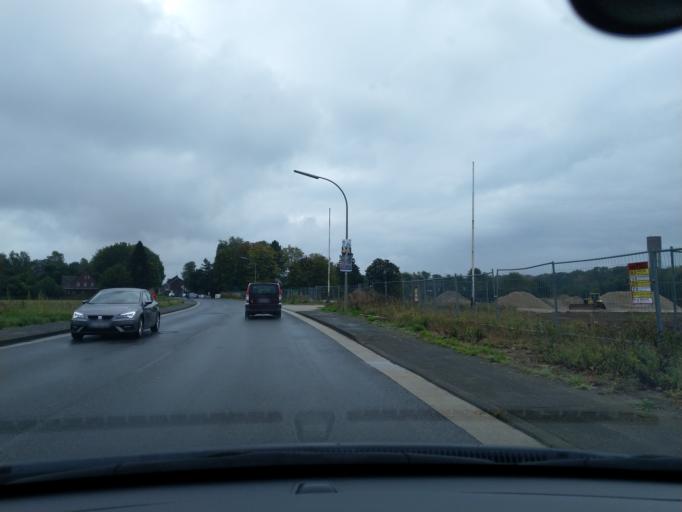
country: DE
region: North Rhine-Westphalia
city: Wegberg
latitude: 51.1302
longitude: 6.2845
